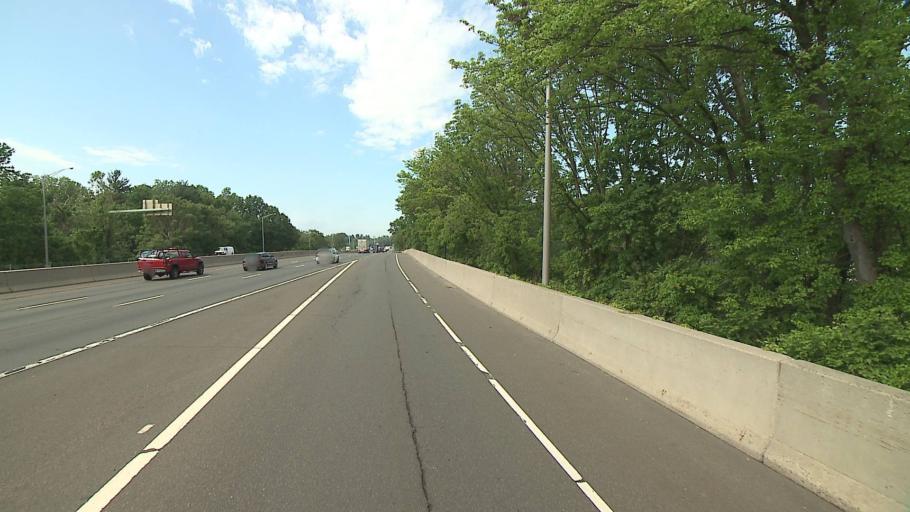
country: US
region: Connecticut
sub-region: Fairfield County
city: Southport
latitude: 41.1351
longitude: -73.2933
